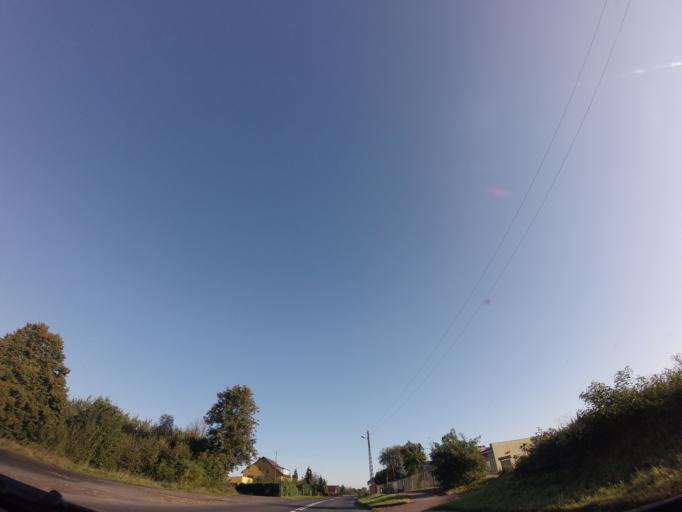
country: PL
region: West Pomeranian Voivodeship
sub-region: Powiat stargardzki
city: Stargard Szczecinski
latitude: 53.3846
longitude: 15.0819
